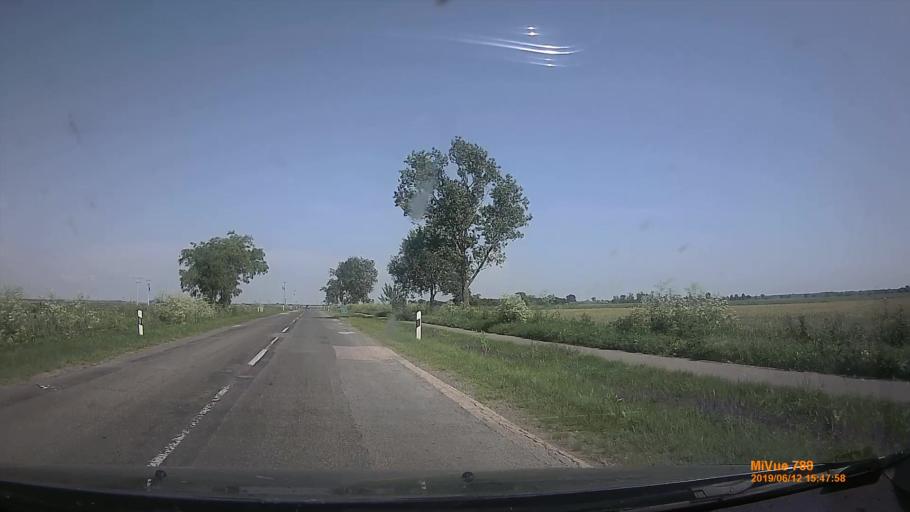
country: HU
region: Csongrad
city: Apatfalva
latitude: 46.2049
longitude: 20.5414
